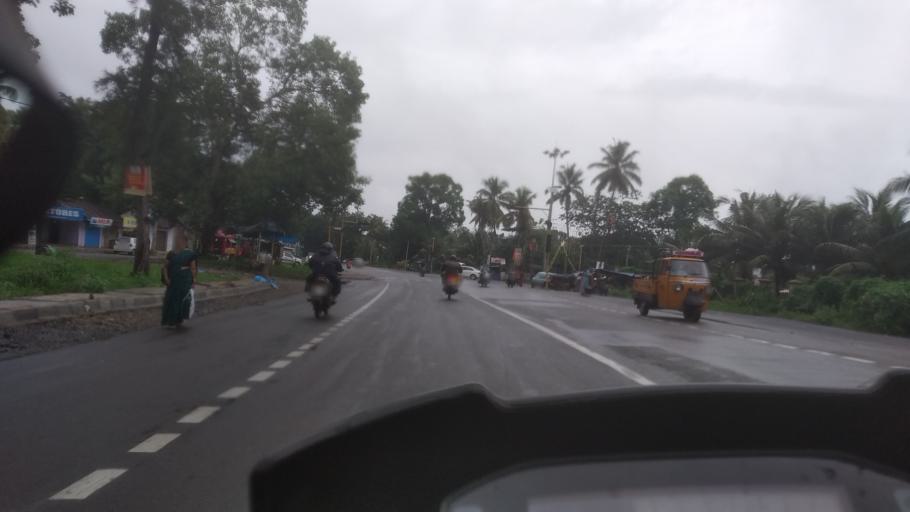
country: IN
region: Kerala
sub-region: Alappuzha
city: Kayankulam
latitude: 9.1502
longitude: 76.5132
